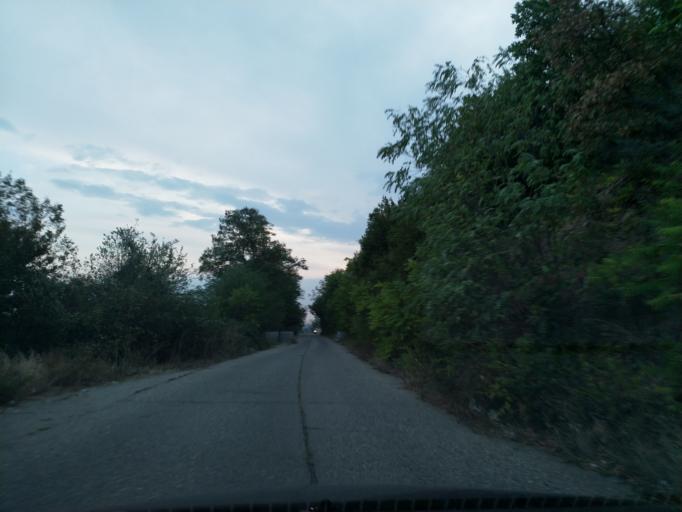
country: RS
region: Central Serbia
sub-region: Pomoravski Okrug
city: Paracin
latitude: 43.8653
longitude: 21.4545
